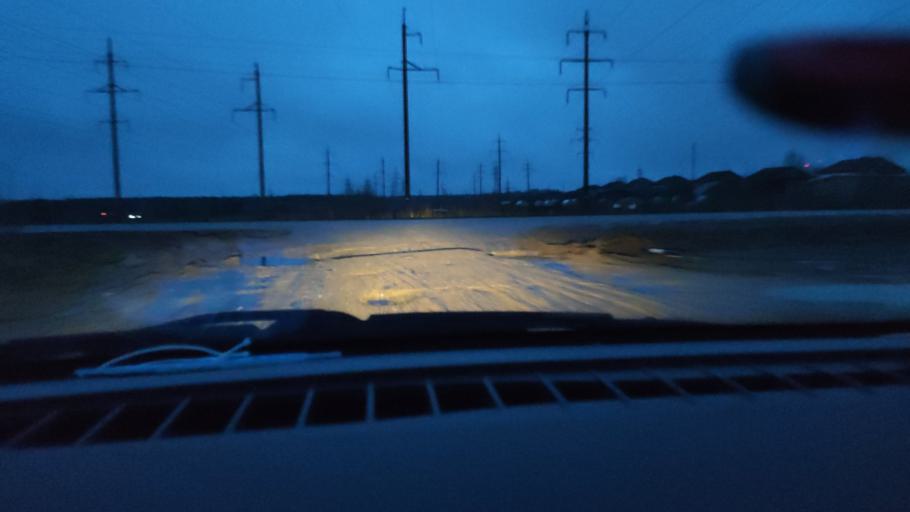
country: RU
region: Udmurtiya
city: Mozhga
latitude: 56.4346
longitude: 52.2514
